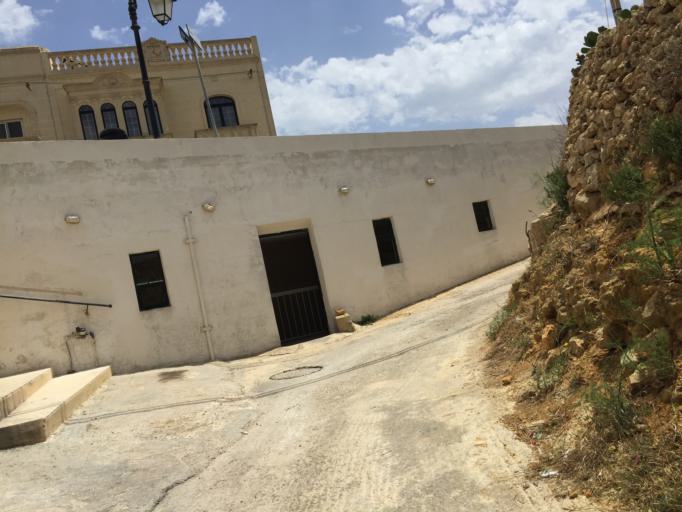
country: MT
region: Iz-Zebbug
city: Zebbug
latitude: 36.0690
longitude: 14.2354
